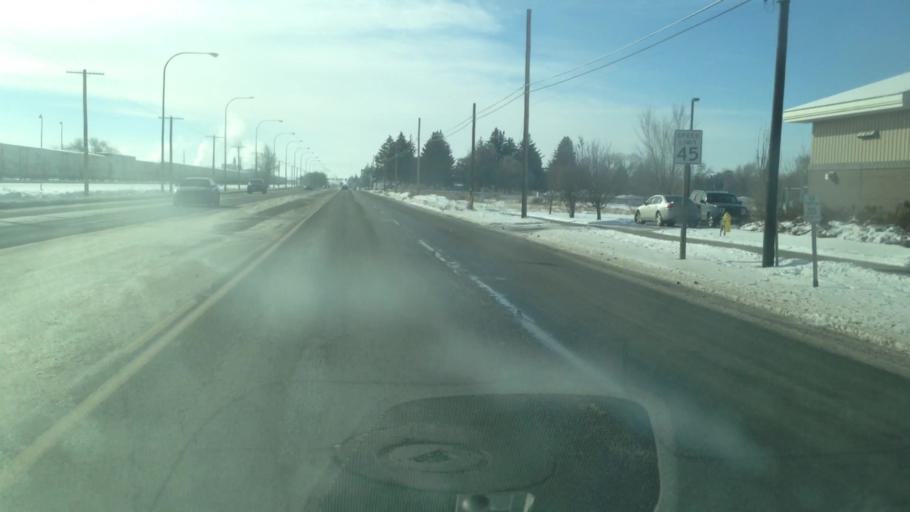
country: US
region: Idaho
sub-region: Bonneville County
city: Idaho Falls
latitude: 43.4753
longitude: -112.0510
